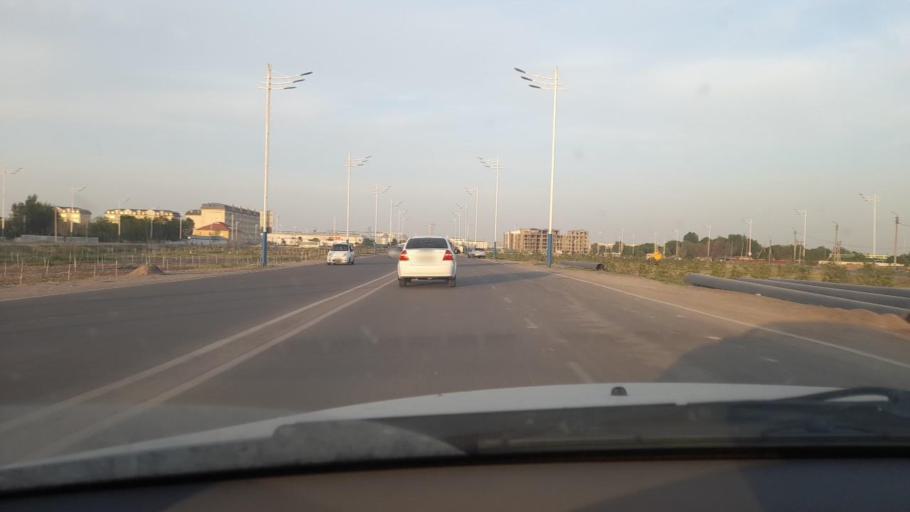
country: UZ
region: Sirdaryo
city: Guliston
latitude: 40.5073
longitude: 68.7547
